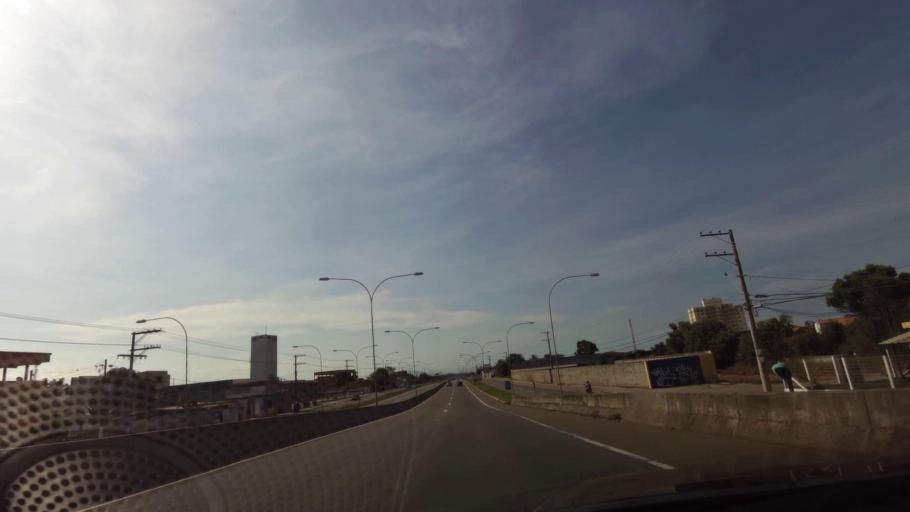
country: BR
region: Espirito Santo
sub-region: Vila Velha
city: Vila Velha
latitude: -20.4464
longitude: -40.3337
